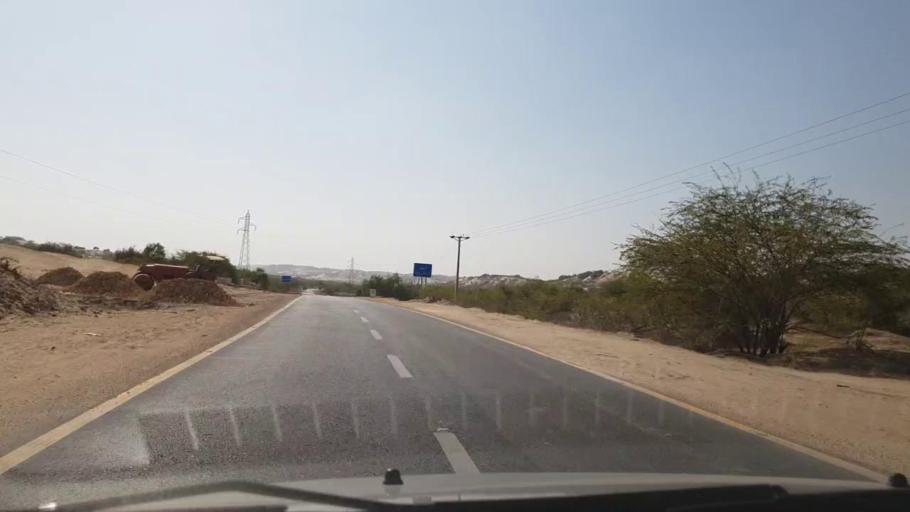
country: PK
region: Sindh
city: Diplo
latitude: 24.4901
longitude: 69.5909
